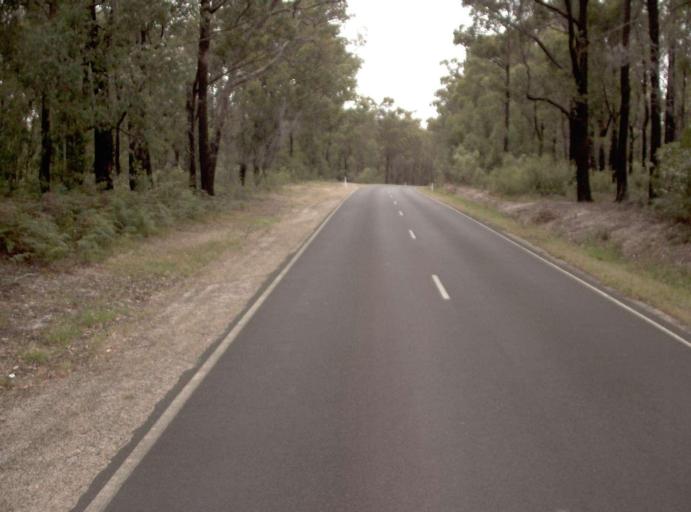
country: AU
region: Victoria
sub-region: Latrobe
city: Traralgon
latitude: -38.4702
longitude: 146.8226
